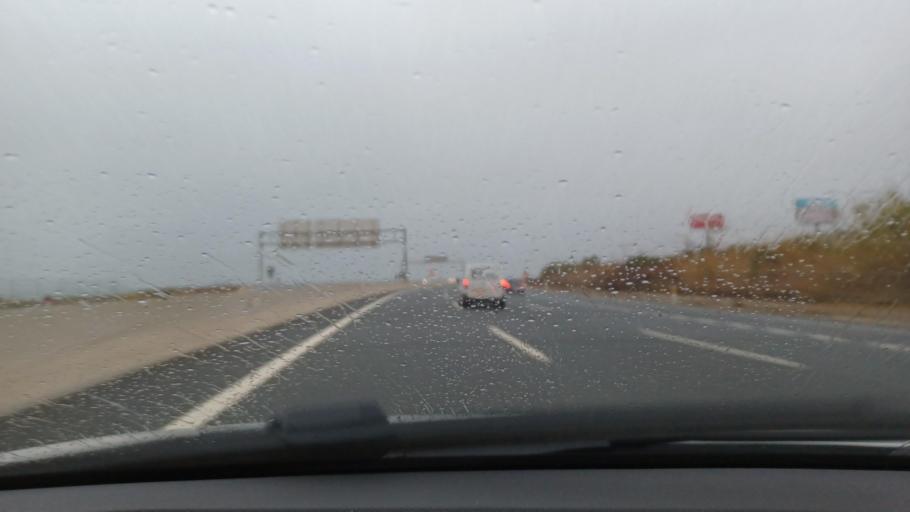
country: ES
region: Valencia
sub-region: Provincia de Valencia
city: Albuixech
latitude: 39.5490
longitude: -0.2980
